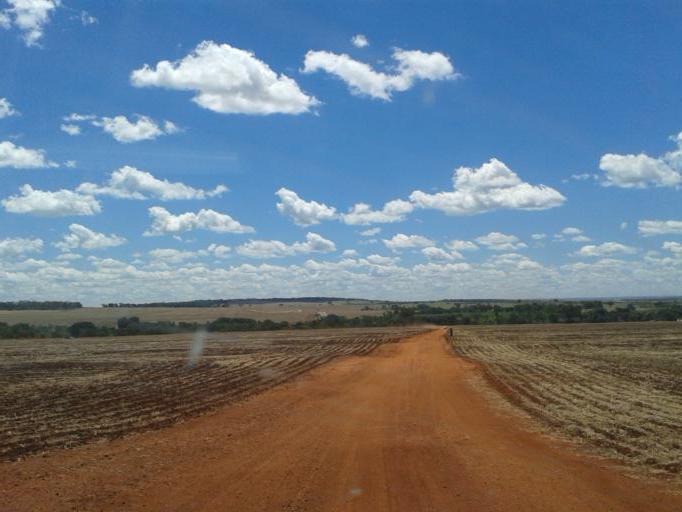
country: BR
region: Minas Gerais
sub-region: Capinopolis
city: Capinopolis
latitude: -18.6130
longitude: -49.5294
